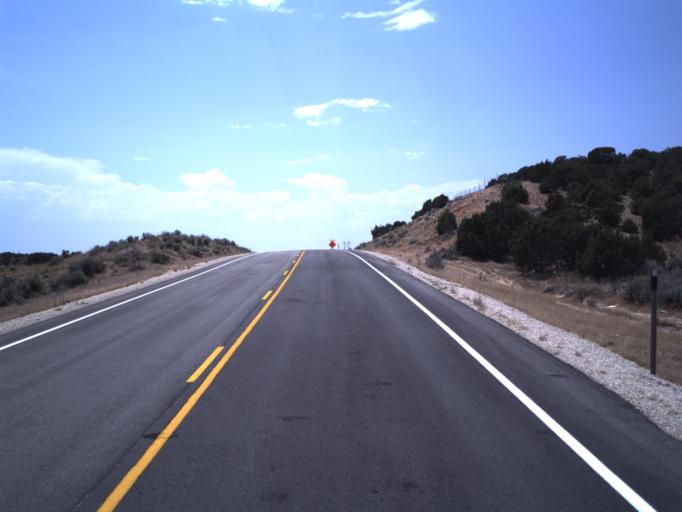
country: US
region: Utah
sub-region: Uintah County
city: Maeser
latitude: 40.4422
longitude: -109.6400
